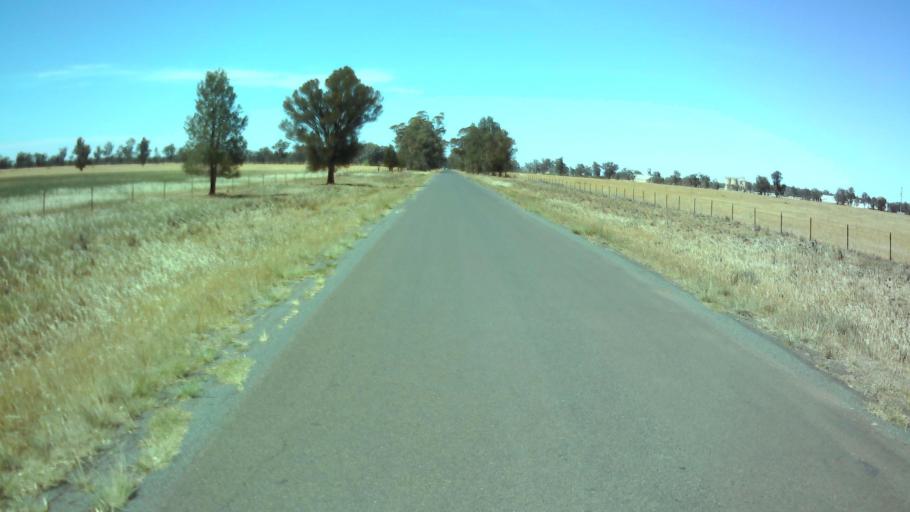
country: AU
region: New South Wales
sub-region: Weddin
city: Grenfell
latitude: -34.1066
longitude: 147.8865
